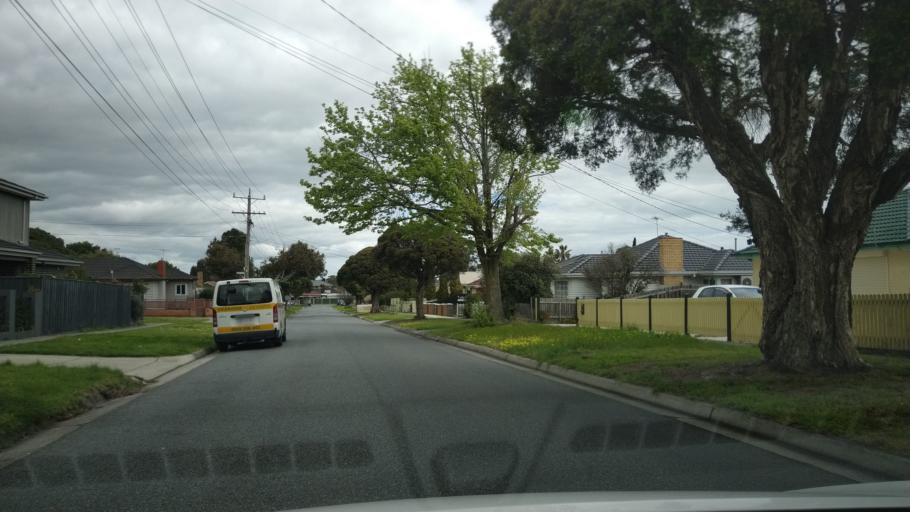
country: AU
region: Victoria
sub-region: Greater Dandenong
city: Noble Park
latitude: -37.9730
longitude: 145.1692
